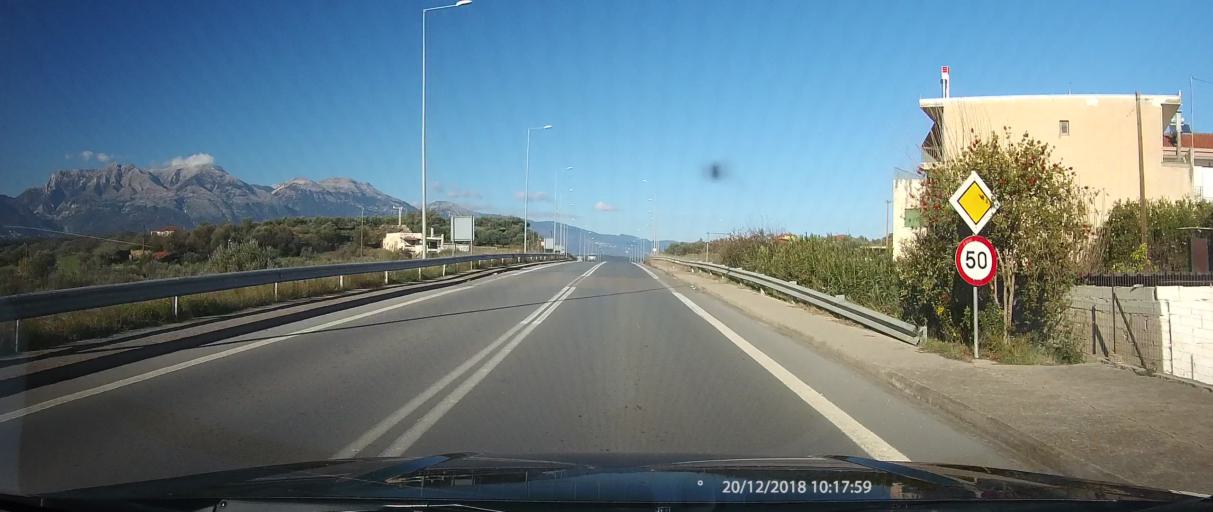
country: GR
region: Peloponnese
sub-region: Nomos Lakonias
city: Sparti
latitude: 37.1124
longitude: 22.4317
